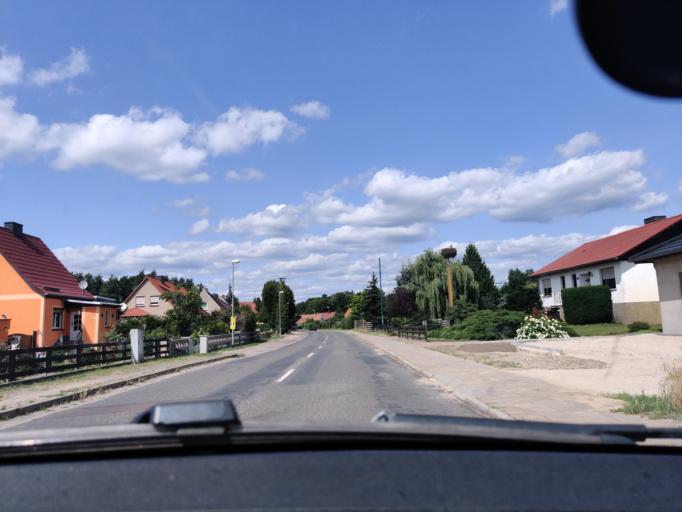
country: DE
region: Saxony-Anhalt
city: Loburg
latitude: 52.1117
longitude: 12.0705
